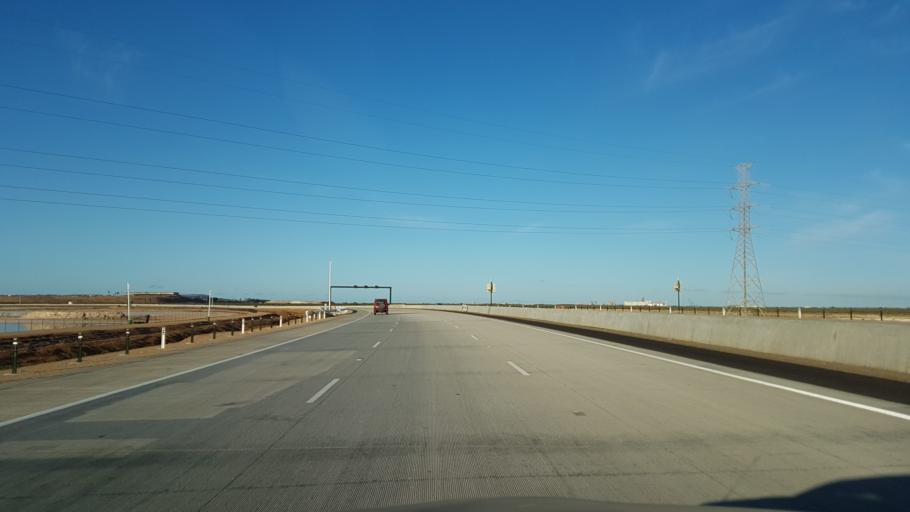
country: AU
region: South Australia
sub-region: Port Adelaide Enfield
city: Enfield
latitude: -34.8098
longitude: 138.5666
